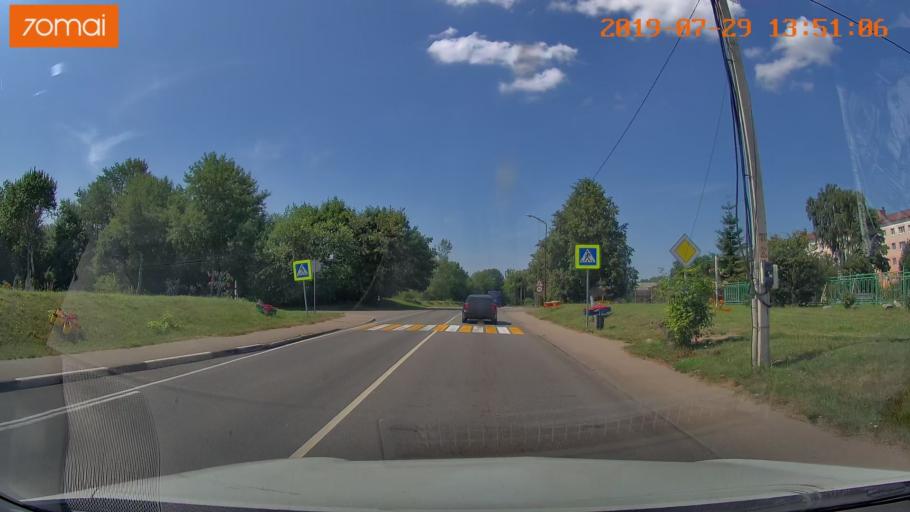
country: RU
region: Kaliningrad
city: Primorsk
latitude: 54.7289
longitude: 20.0062
